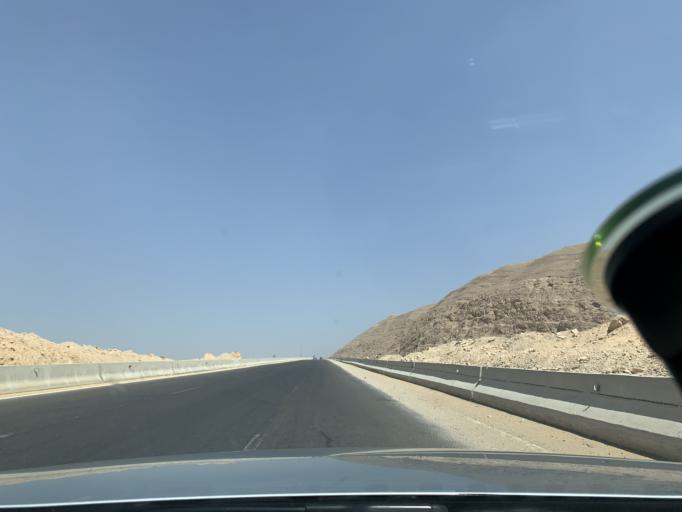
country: EG
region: As Suways
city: Ain Sukhna
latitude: 29.5523
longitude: 32.2779
